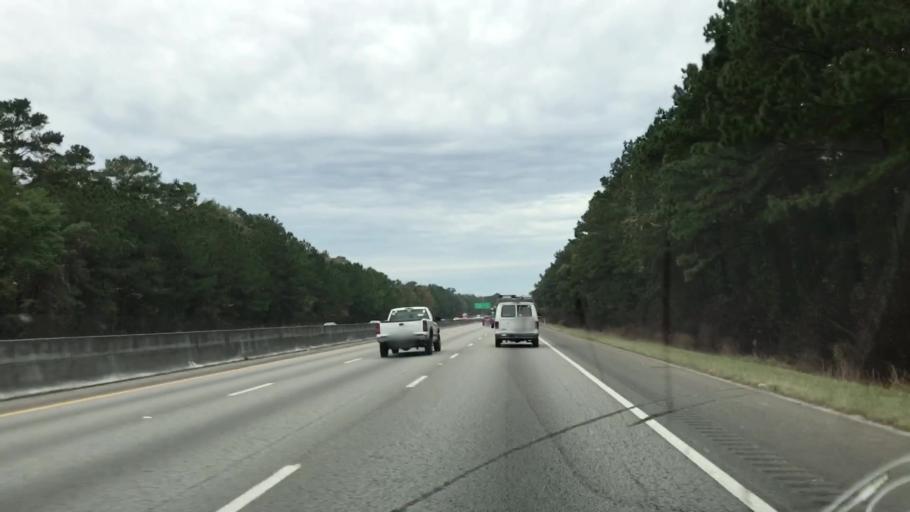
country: US
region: South Carolina
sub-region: Berkeley County
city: Goose Creek
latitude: 32.9561
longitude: -80.0662
